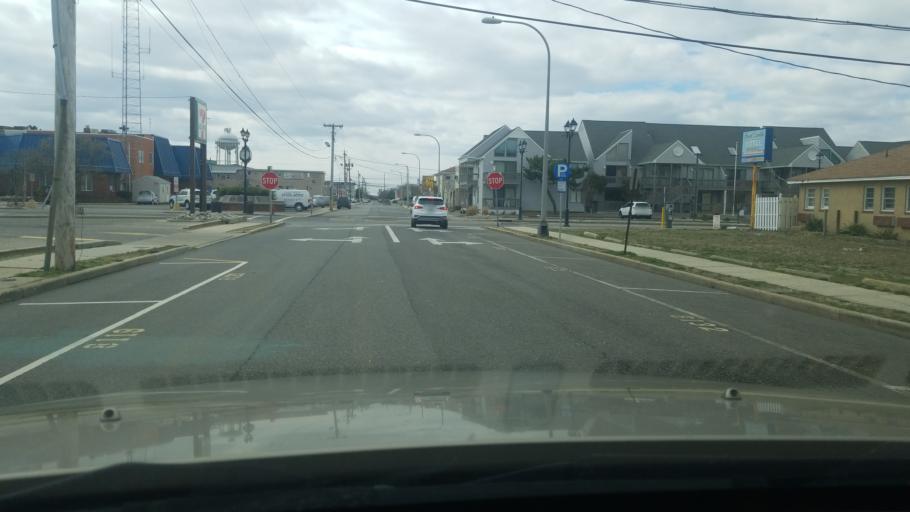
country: US
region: New Jersey
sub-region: Ocean County
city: Seaside Heights
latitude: 39.9440
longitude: -74.0727
